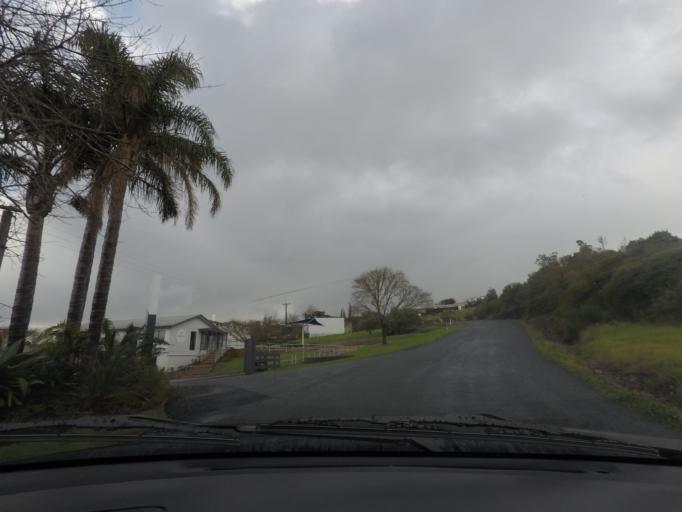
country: NZ
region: Auckland
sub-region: Auckland
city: Warkworth
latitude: -36.4292
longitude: 174.7313
